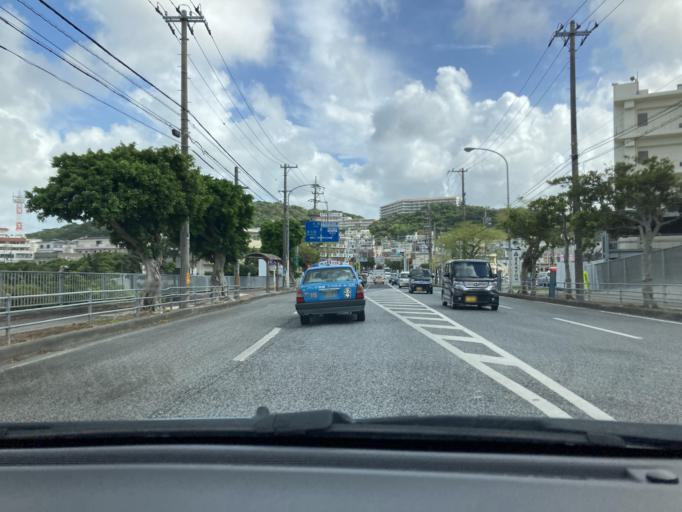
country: JP
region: Okinawa
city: Tomigusuku
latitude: 26.1780
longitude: 127.6816
